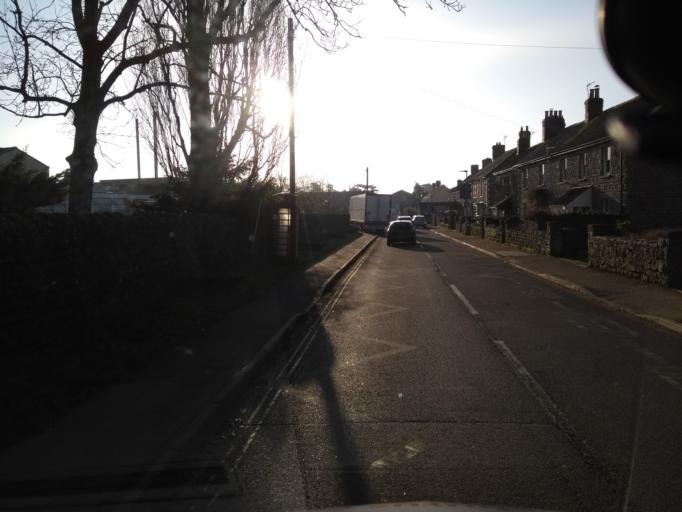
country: GB
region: England
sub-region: Somerset
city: Evercreech
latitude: 51.1497
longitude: -2.5070
